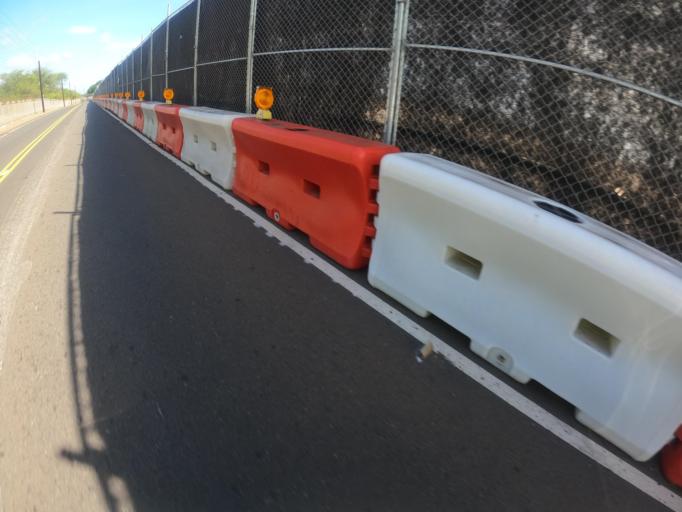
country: US
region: Hawaii
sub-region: Honolulu County
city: Makakilo City
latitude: 21.3246
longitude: -158.0842
